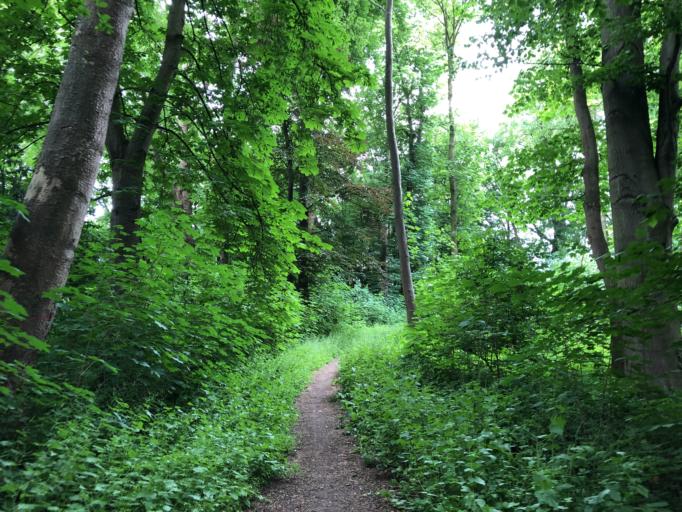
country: DE
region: North Rhine-Westphalia
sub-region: Regierungsbezirk Dusseldorf
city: Erkrath
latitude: 51.1941
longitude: 6.8551
